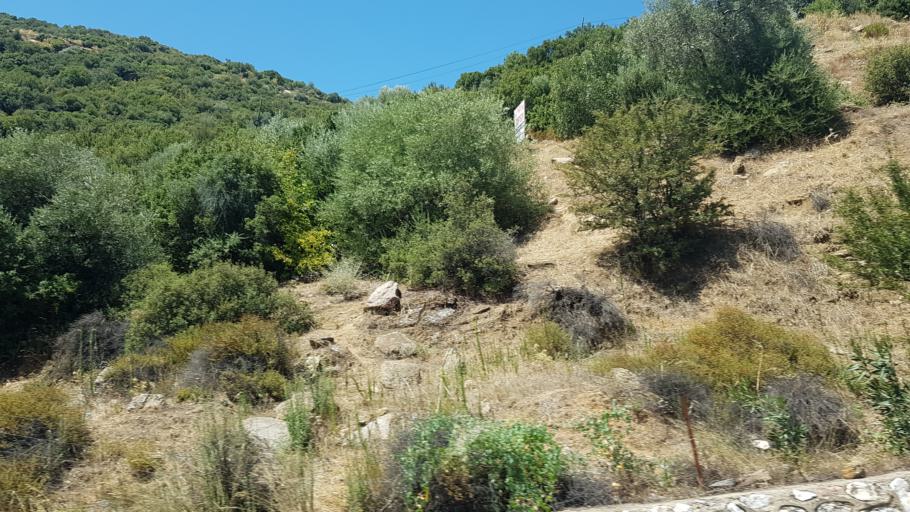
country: TR
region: Aydin
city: Akcaova
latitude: 37.5056
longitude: 28.1027
